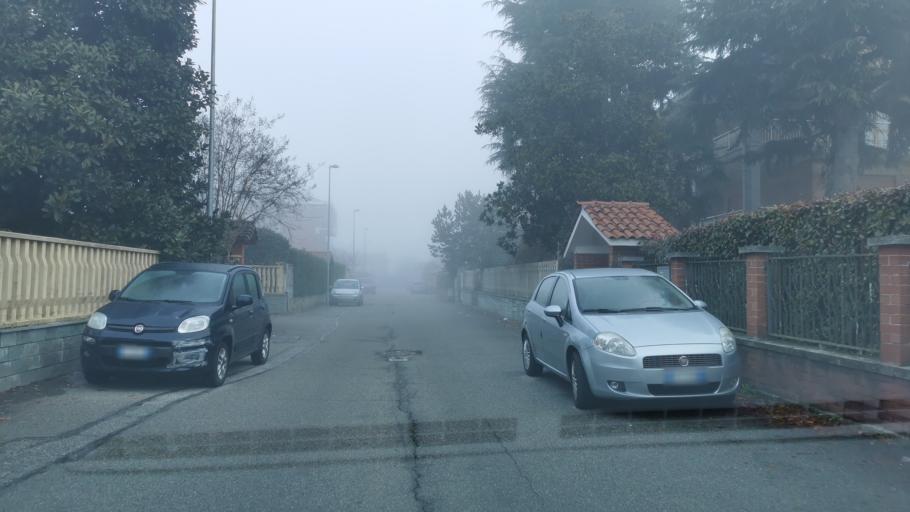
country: IT
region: Piedmont
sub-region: Provincia di Torino
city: Volpiano
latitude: 45.1952
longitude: 7.7648
